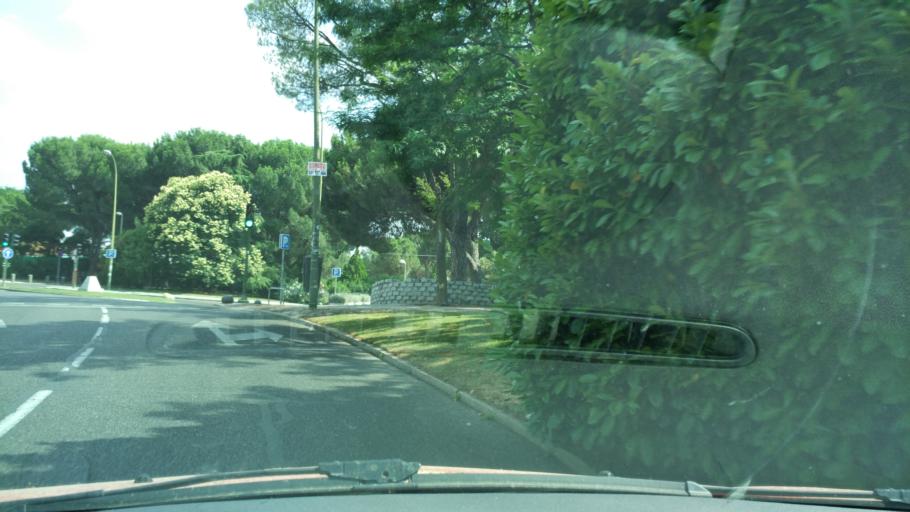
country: ES
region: Madrid
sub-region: Provincia de Madrid
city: Tetuan de las Victorias
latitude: 40.4600
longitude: -3.7197
